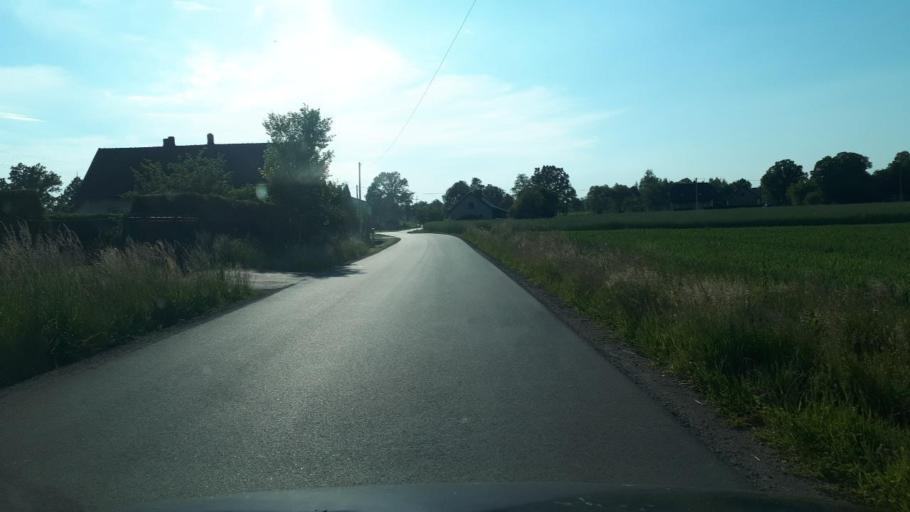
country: PL
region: Silesian Voivodeship
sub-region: Powiat bielski
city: Bronow
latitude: 49.8703
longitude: 18.9324
